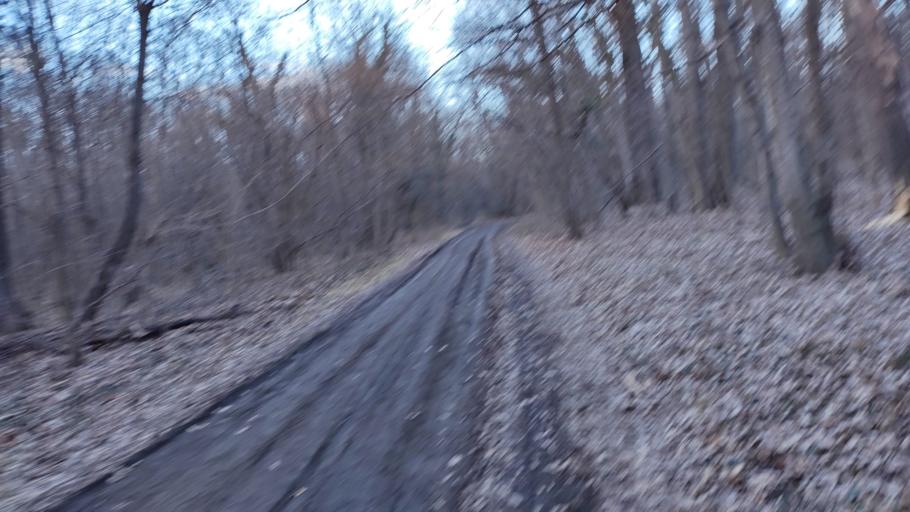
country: RO
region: Ilfov
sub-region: Comuna Otopeni
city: Otopeni
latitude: 44.5292
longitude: 26.0829
